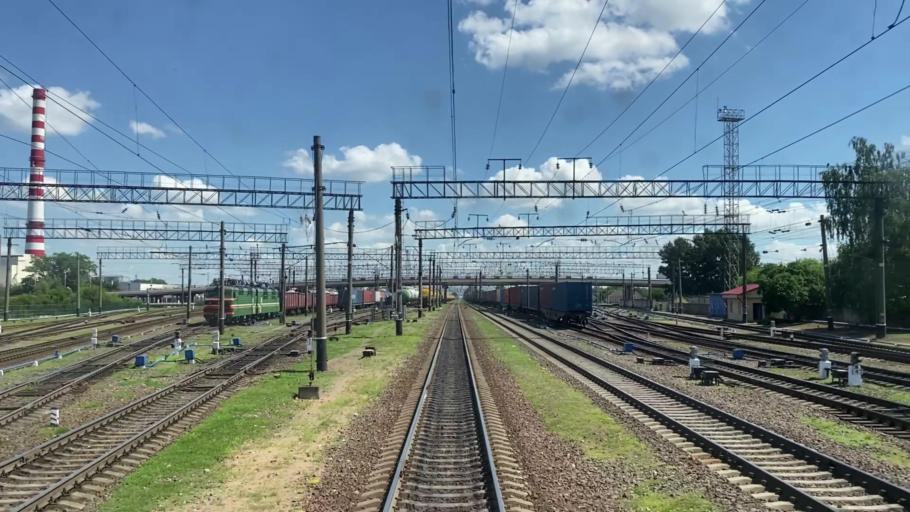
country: BY
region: Brest
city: Baranovichi
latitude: 53.1377
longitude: 26.0071
